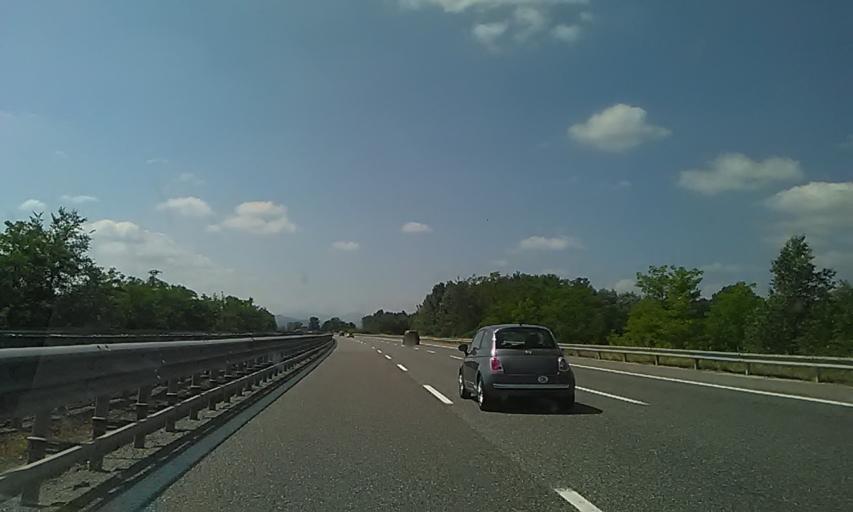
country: IT
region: Piedmont
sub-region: Provincia di Alessandria
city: Capriata d'Orba
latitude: 44.7161
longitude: 8.6666
